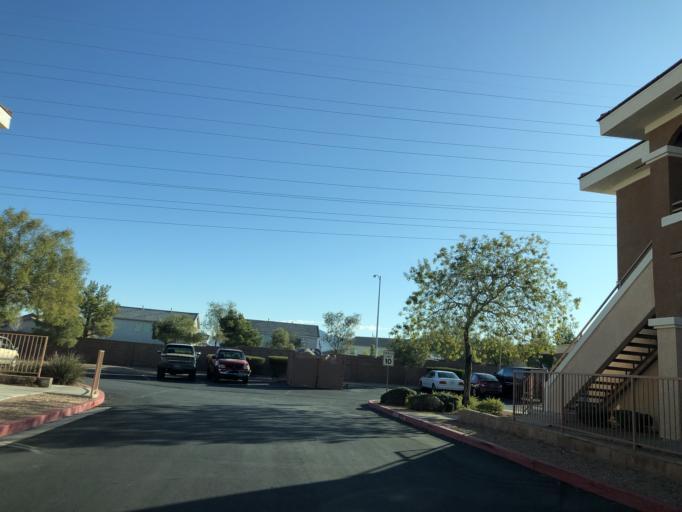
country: US
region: Nevada
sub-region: Clark County
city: Whitney
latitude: 36.0010
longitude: -115.0908
